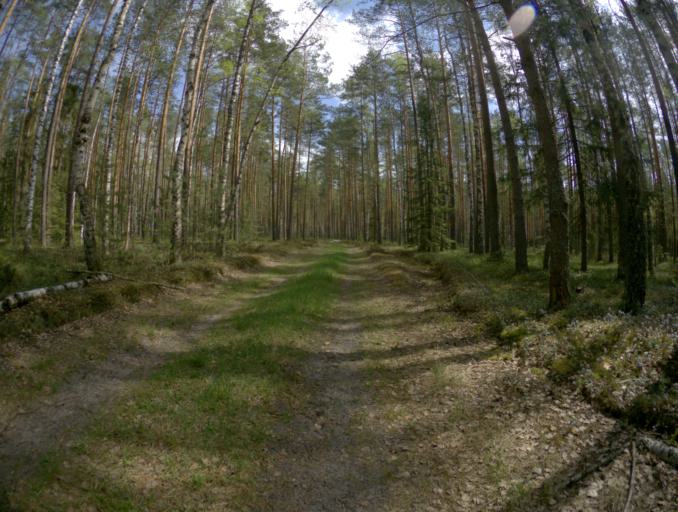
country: RU
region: Vladimir
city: Golovino
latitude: 55.9298
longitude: 40.3715
